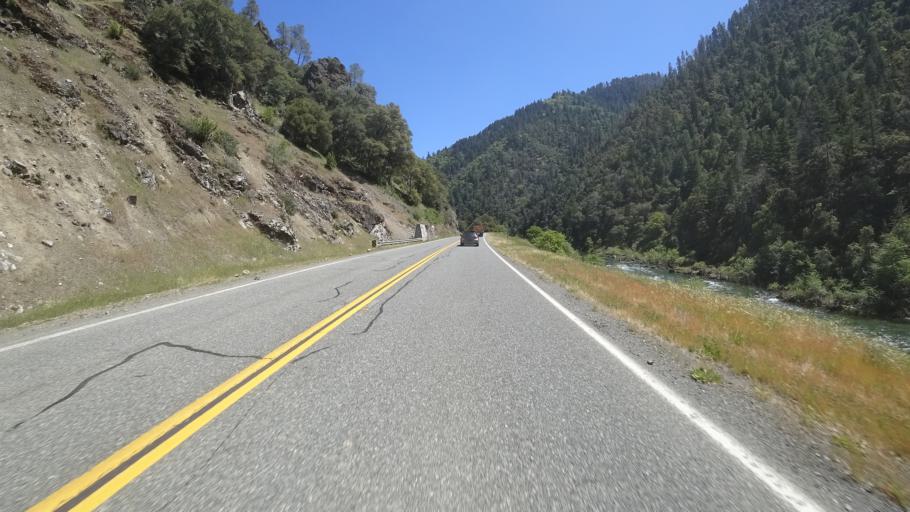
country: US
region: California
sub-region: Humboldt County
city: Willow Creek
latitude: 40.7952
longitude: -123.3780
